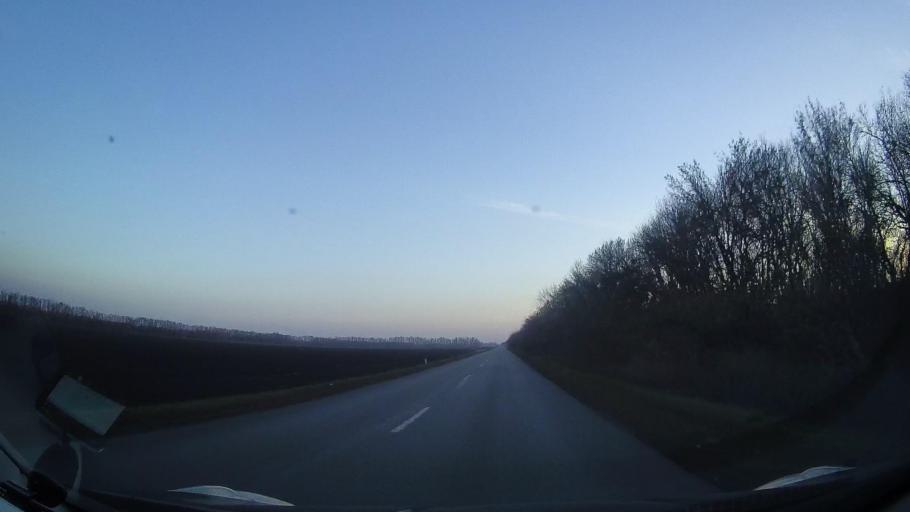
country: RU
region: Rostov
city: Zernograd
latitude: 47.0178
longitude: 40.3916
